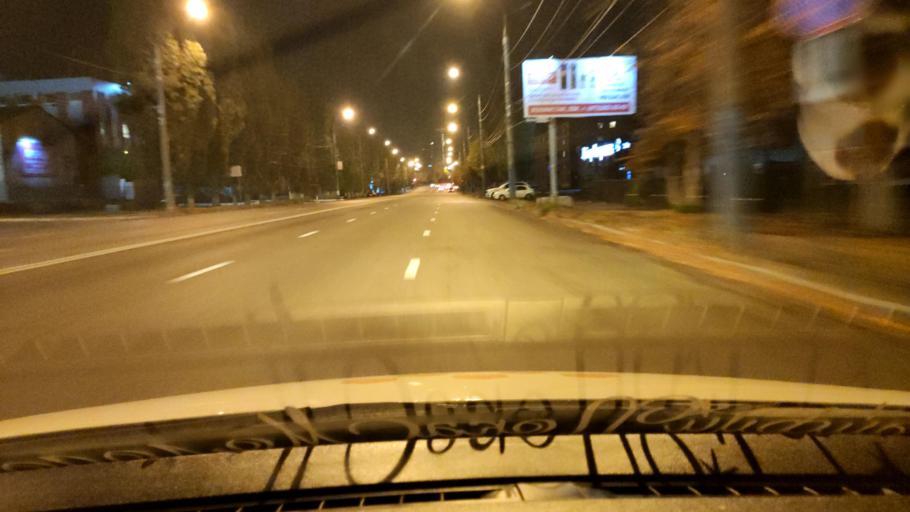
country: RU
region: Voronezj
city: Voronezh
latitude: 51.6853
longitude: 39.1656
